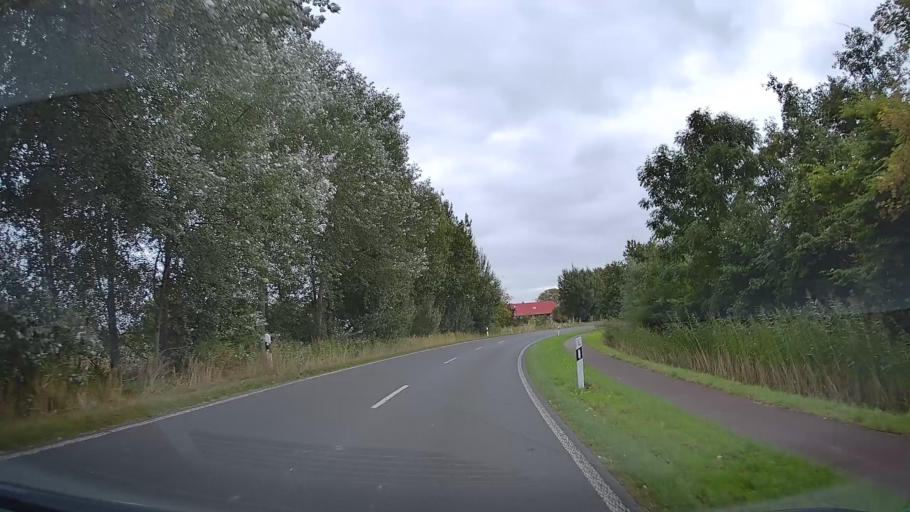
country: DE
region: Schleswig-Holstein
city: Klanxbull
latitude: 54.8668
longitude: 8.6765
